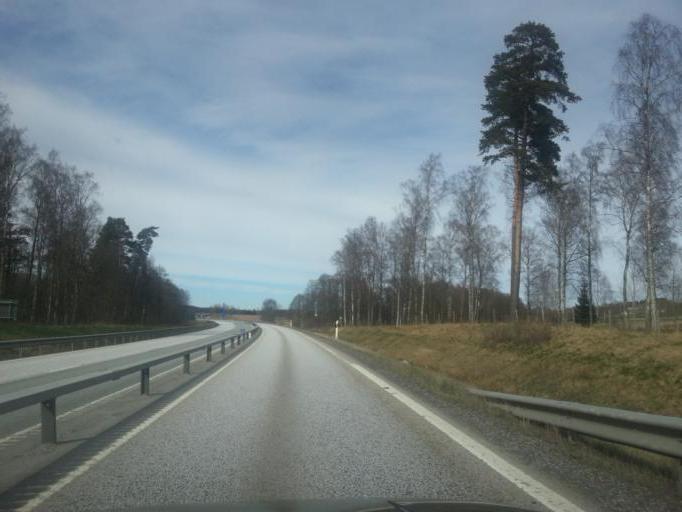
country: SE
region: Joenkoeping
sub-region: Jonkopings Kommun
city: Bankeryd
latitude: 57.8217
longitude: 14.1036
